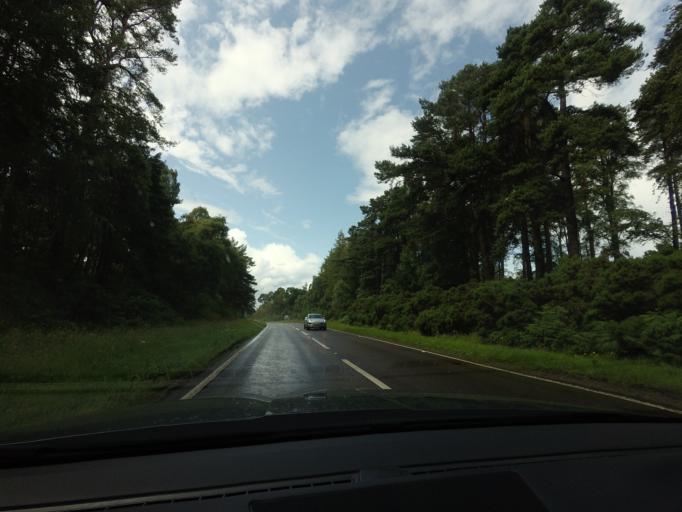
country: GB
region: Scotland
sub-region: Moray
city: Lhanbryd
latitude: 57.6332
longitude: -3.1862
